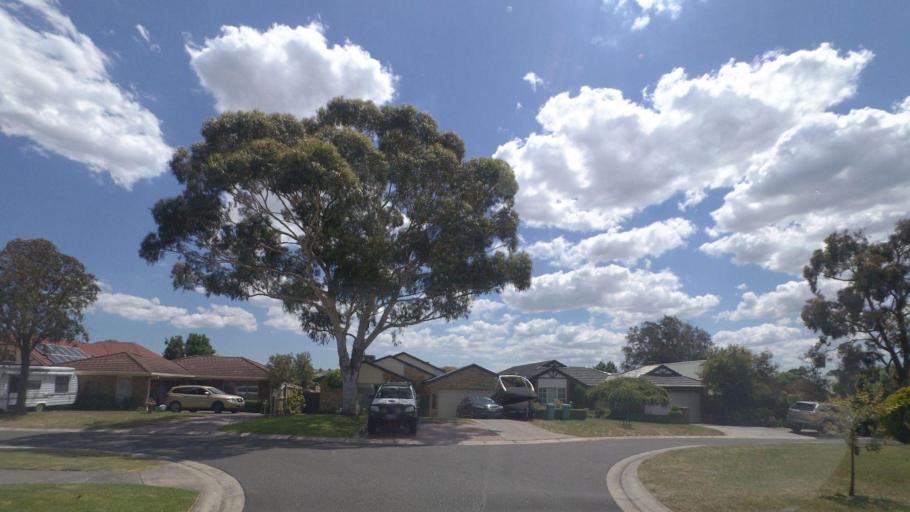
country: AU
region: Victoria
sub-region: Knox
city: Knoxfield
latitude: -37.8763
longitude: 145.2486
